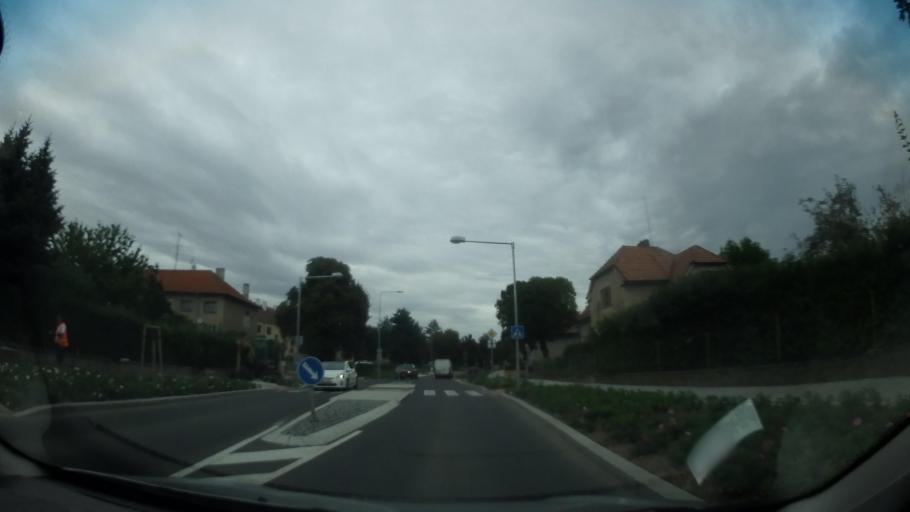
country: CZ
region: Central Bohemia
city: Lysa nad Labem
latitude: 50.2061
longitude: 14.8433
